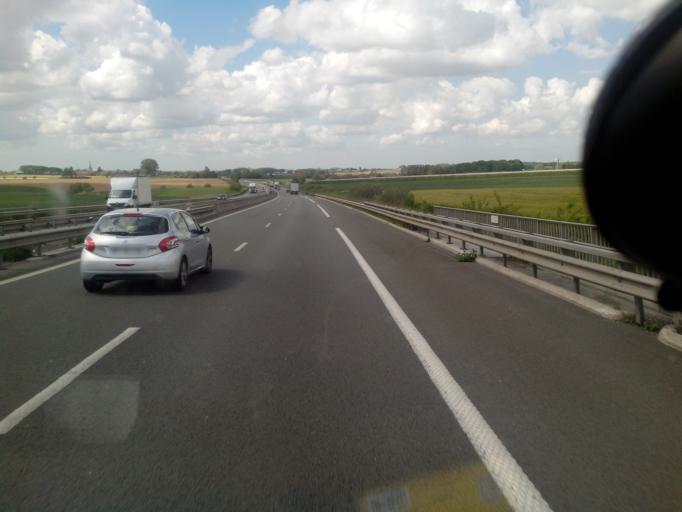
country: FR
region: Nord-Pas-de-Calais
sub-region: Departement du Nord
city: Godewaersvelde
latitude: 50.7884
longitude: 2.6213
